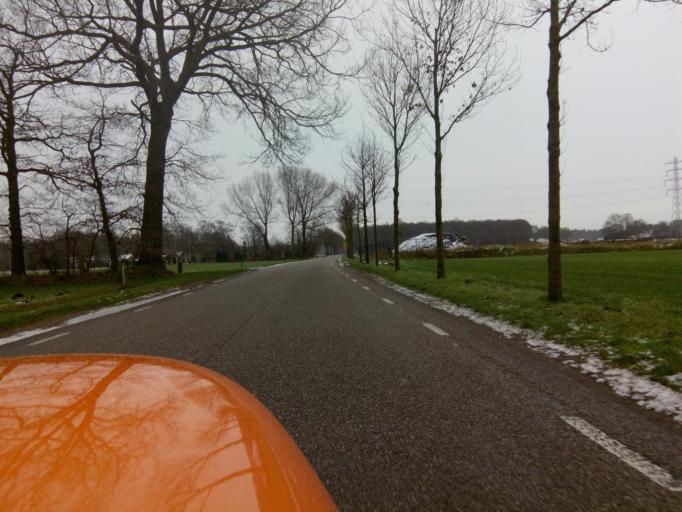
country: NL
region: Gelderland
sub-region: Gemeente Putten
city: Putten
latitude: 52.2255
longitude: 5.5919
